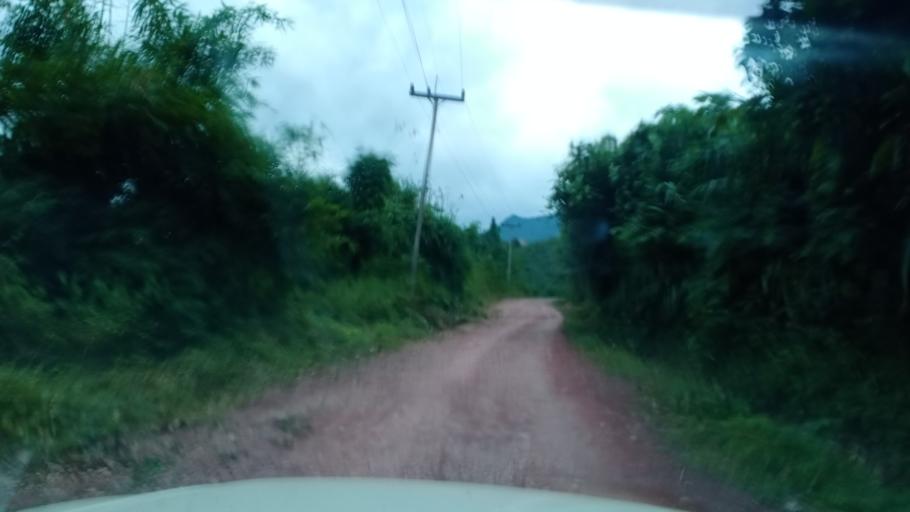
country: TH
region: Changwat Bueng Kan
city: Pak Khat
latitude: 18.7204
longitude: 103.2294
